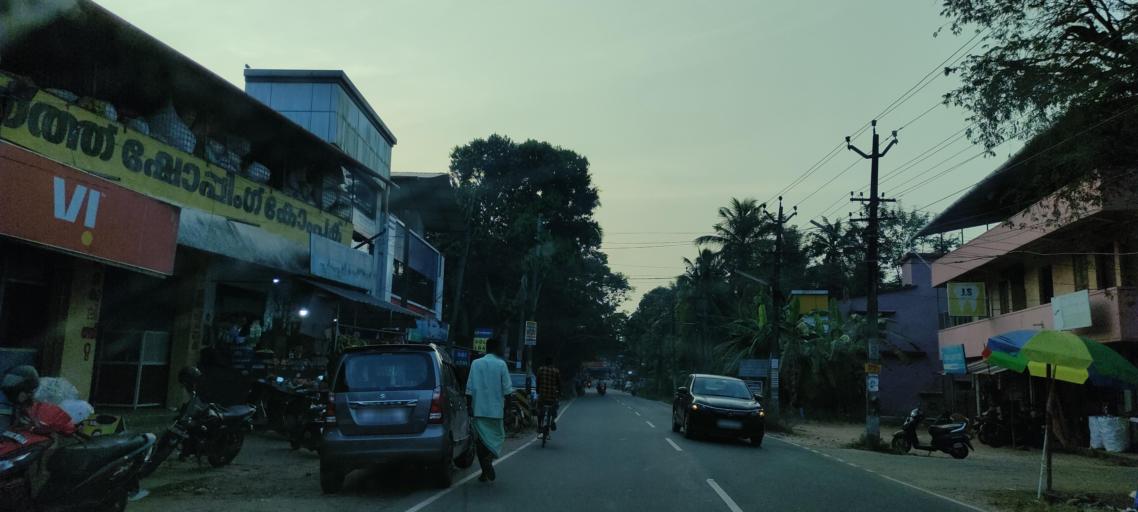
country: IN
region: Kerala
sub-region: Alappuzha
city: Mavelikara
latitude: 9.2790
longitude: 76.5326
